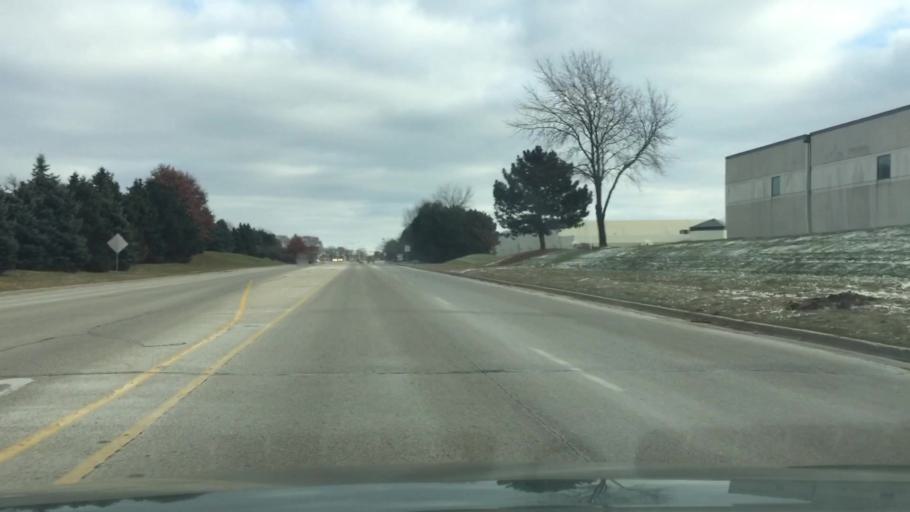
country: US
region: Wisconsin
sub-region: Waukesha County
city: Oconomowoc
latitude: 43.0767
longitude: -88.4777
